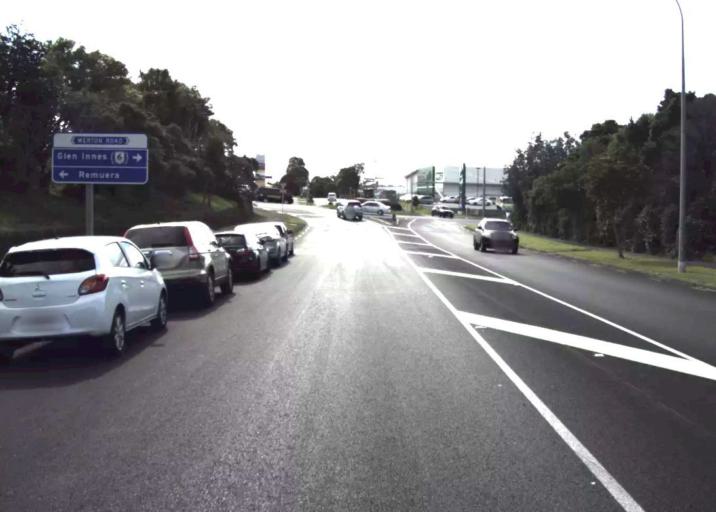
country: NZ
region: Auckland
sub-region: Auckland
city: Tamaki
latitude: -36.8812
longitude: 174.8511
